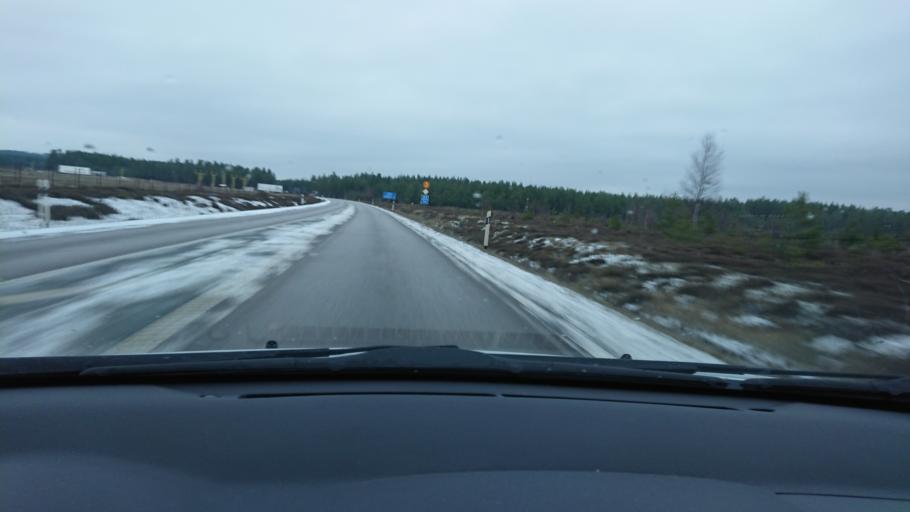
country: SE
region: Kalmar
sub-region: Hultsfreds Kommun
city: Hultsfred
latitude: 57.5191
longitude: 15.8430
